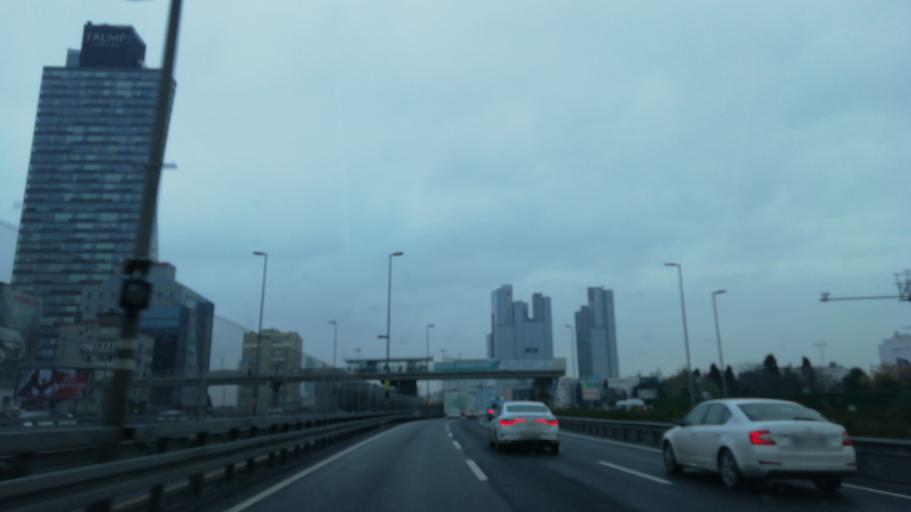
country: TR
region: Istanbul
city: Sisli
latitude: 41.0670
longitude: 28.9894
